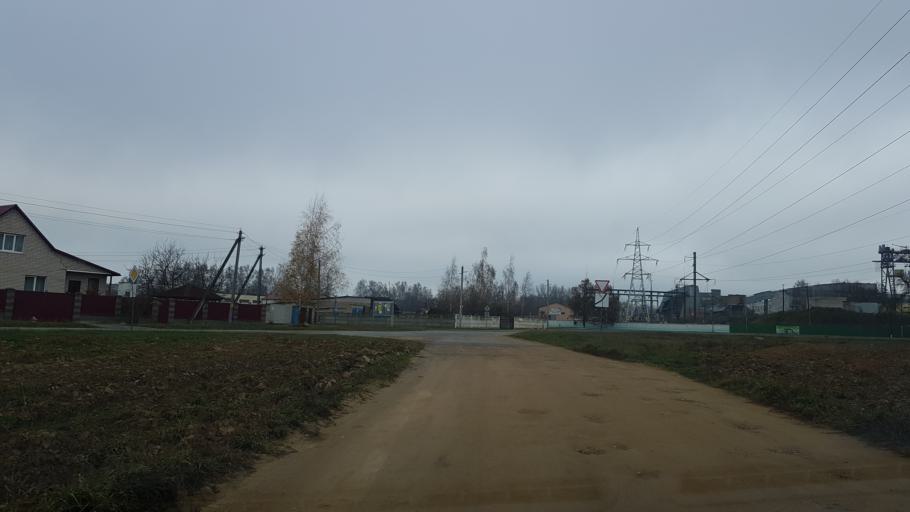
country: BY
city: Fanipol
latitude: 53.7350
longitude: 27.3240
